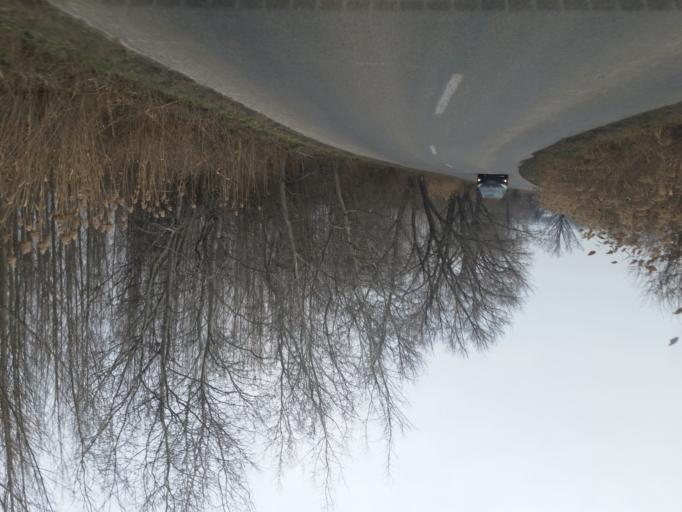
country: HU
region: Pest
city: Perbal
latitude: 47.5790
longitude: 18.7746
